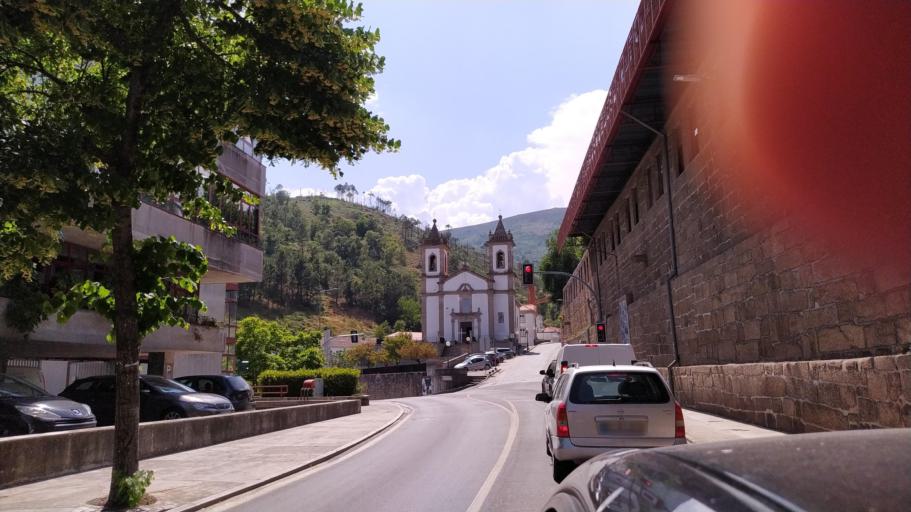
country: PT
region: Castelo Branco
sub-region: Covilha
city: Covilha
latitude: 40.2779
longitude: -7.5091
